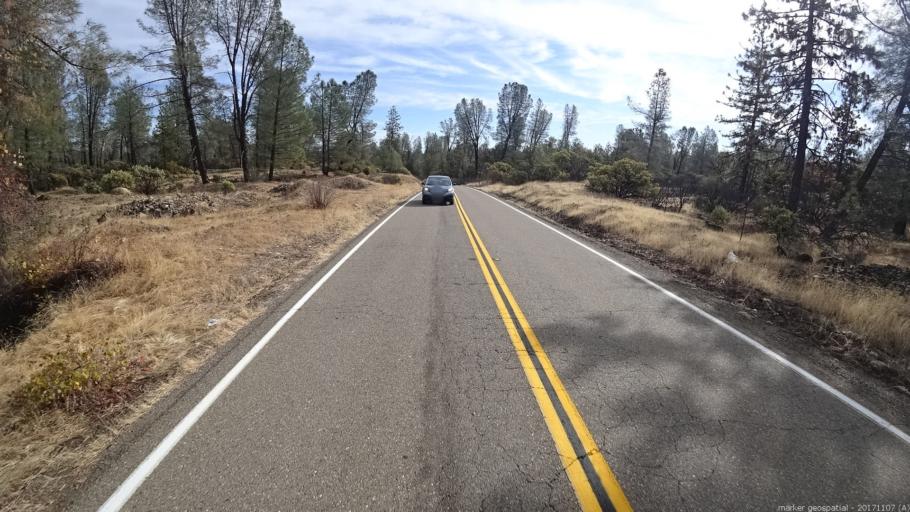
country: US
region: California
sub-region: Shasta County
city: Shasta
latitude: 40.5093
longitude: -122.5303
